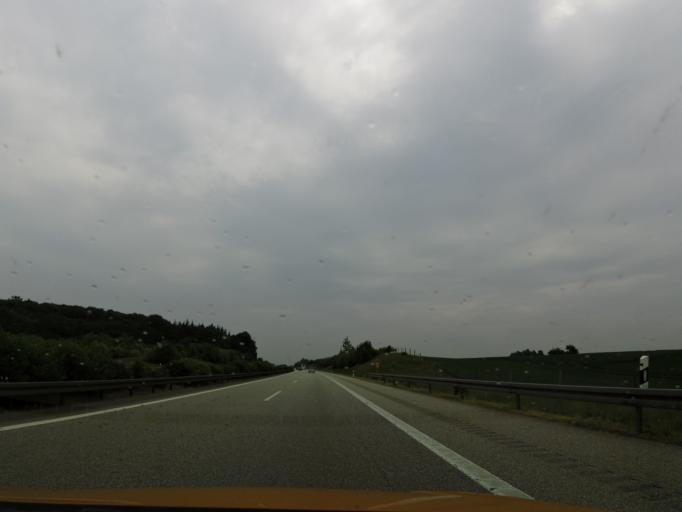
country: DE
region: Mecklenburg-Vorpommern
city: Rehna
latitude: 53.8187
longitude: 11.0986
